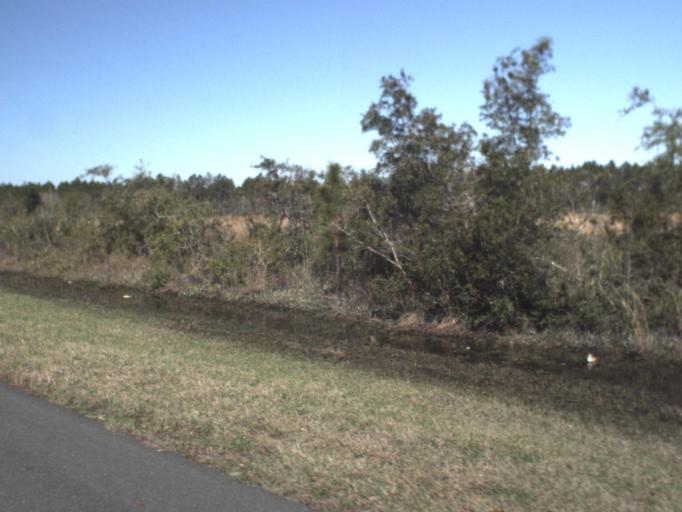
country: US
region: Florida
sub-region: Bay County
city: Callaway
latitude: 30.1519
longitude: -85.4856
